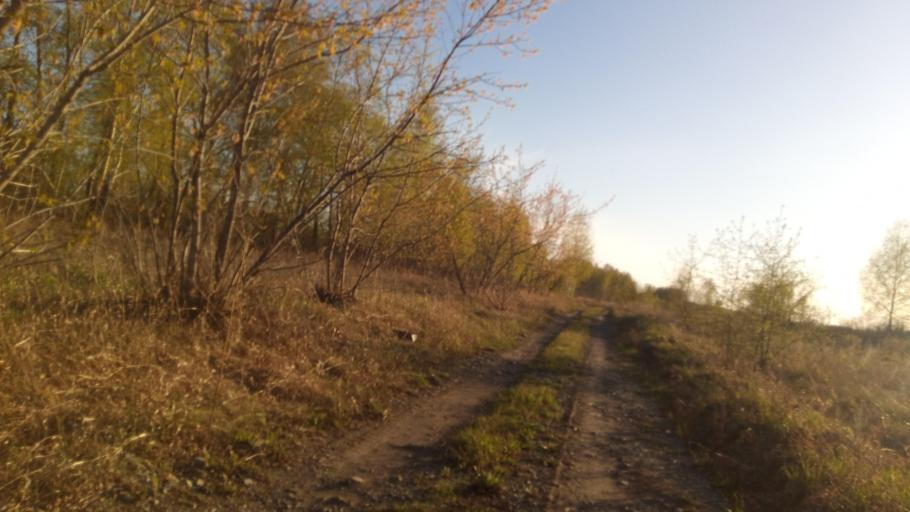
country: RU
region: Chelyabinsk
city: Timiryazevskiy
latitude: 54.9889
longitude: 60.8556
